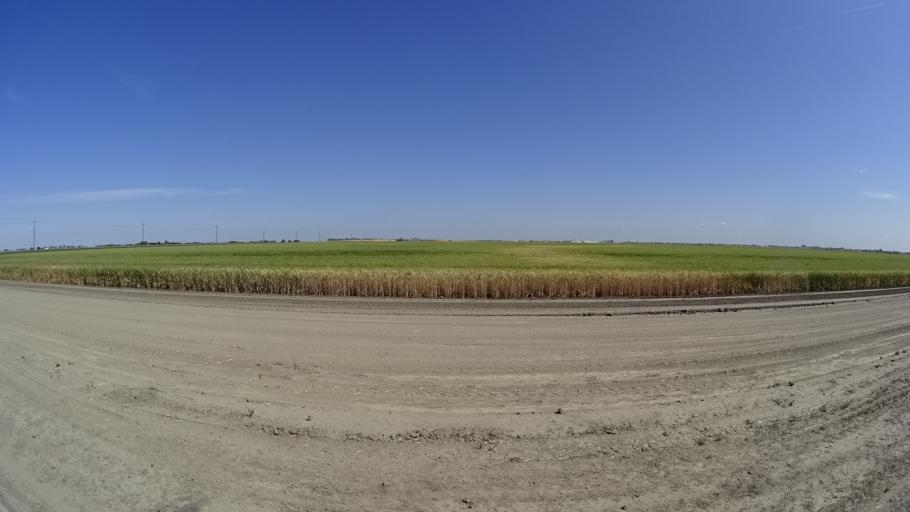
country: US
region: California
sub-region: Kings County
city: Stratford
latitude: 36.2552
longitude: -119.8323
